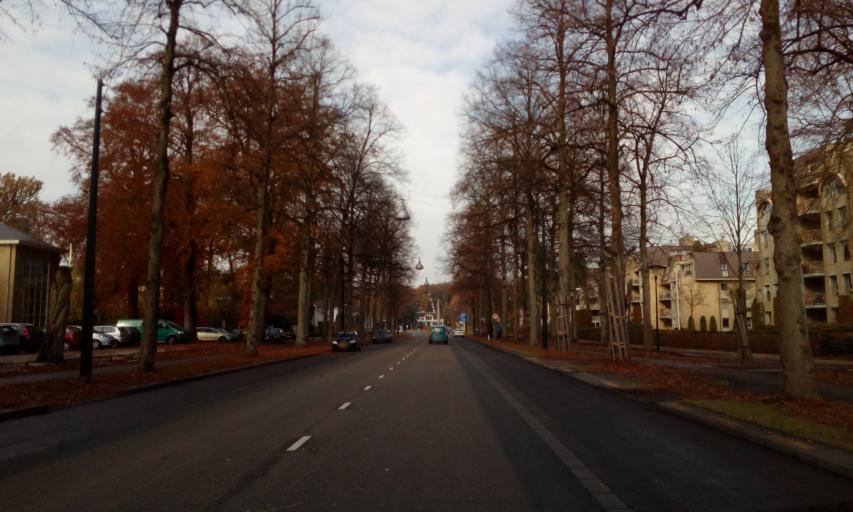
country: NL
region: Gelderland
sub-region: Gemeente Apeldoorn
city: Apeldoorn
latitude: 52.2252
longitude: 5.9495
